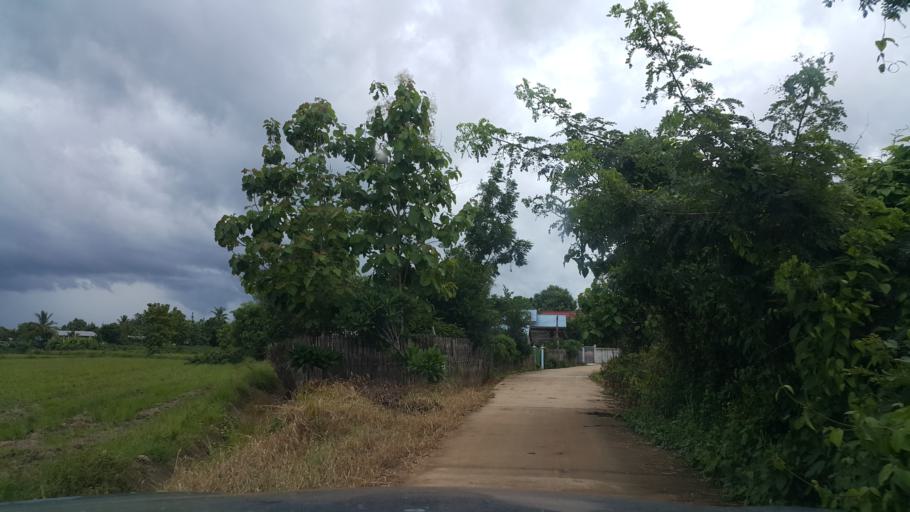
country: TH
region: Sukhothai
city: Thung Saliam
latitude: 17.3190
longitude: 99.5807
